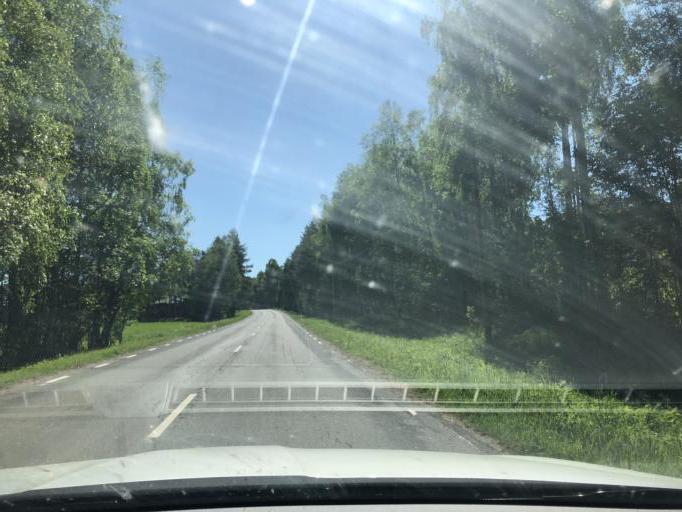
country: SE
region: Norrbotten
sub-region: Lulea Kommun
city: Sodra Sunderbyn
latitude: 65.6630
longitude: 21.9723
